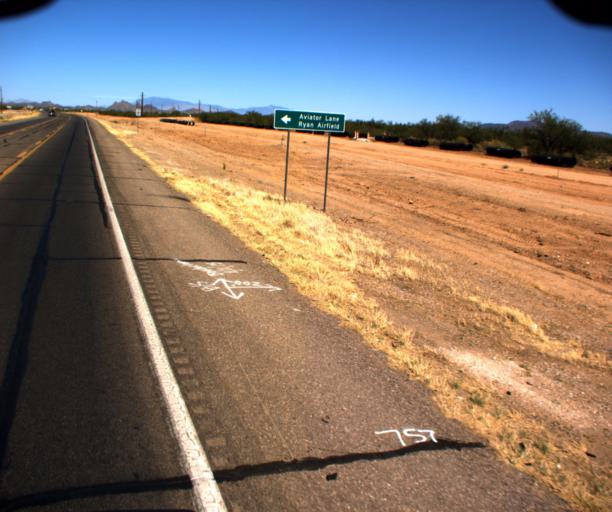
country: US
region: Arizona
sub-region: Pima County
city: Valencia West
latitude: 32.1327
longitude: -111.1759
